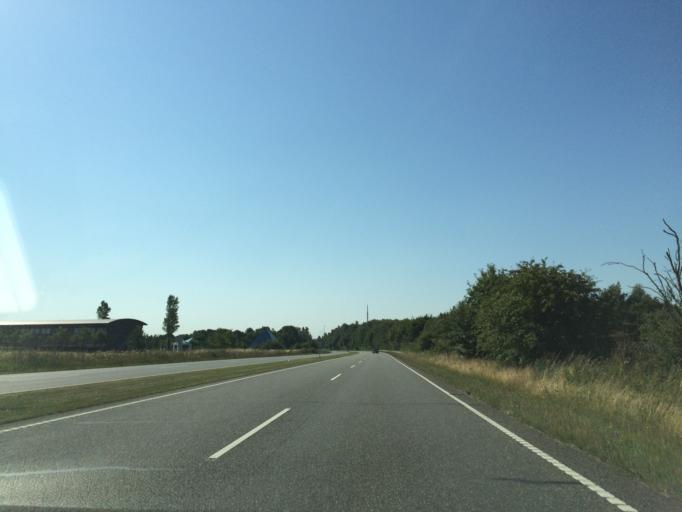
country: DK
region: South Denmark
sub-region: Kolding Kommune
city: Kolding
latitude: 55.5145
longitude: 9.5021
